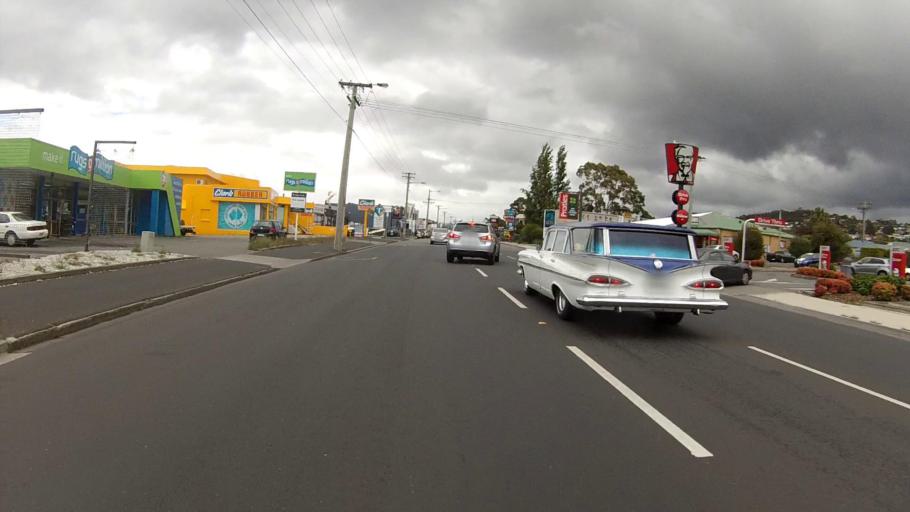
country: AU
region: Tasmania
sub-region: Glenorchy
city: Goodwood
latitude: -42.8371
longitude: 147.2879
